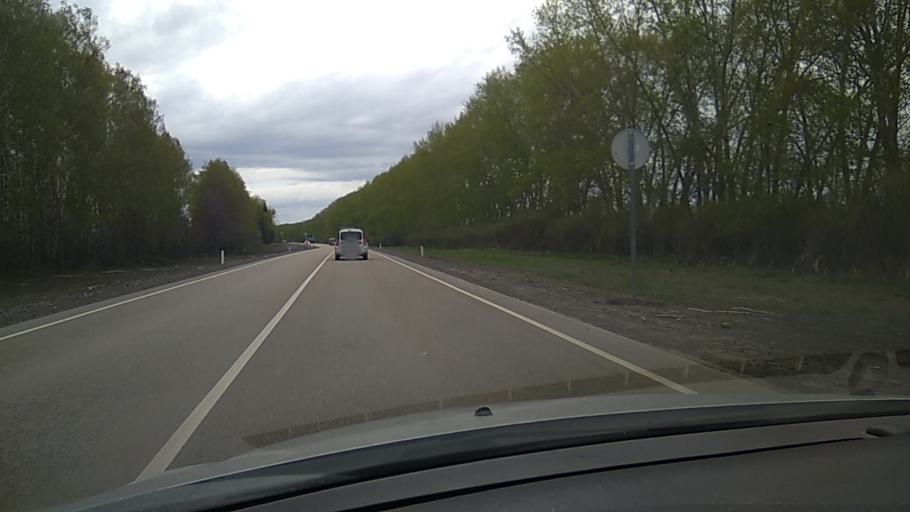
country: RU
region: Sverdlovsk
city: Dvurechensk
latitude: 56.6442
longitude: 61.2154
